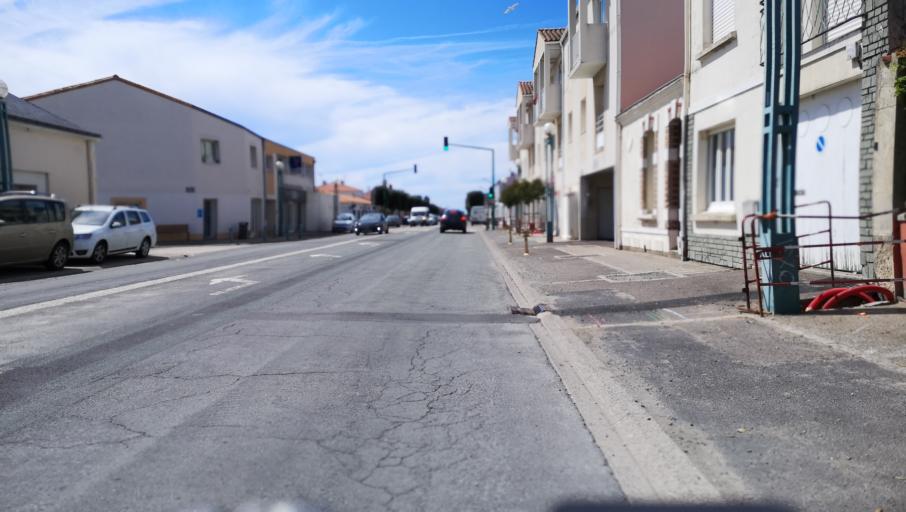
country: FR
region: Pays de la Loire
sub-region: Departement de la Vendee
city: Chateau-d'Olonne
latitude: 46.4922
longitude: -1.7589
